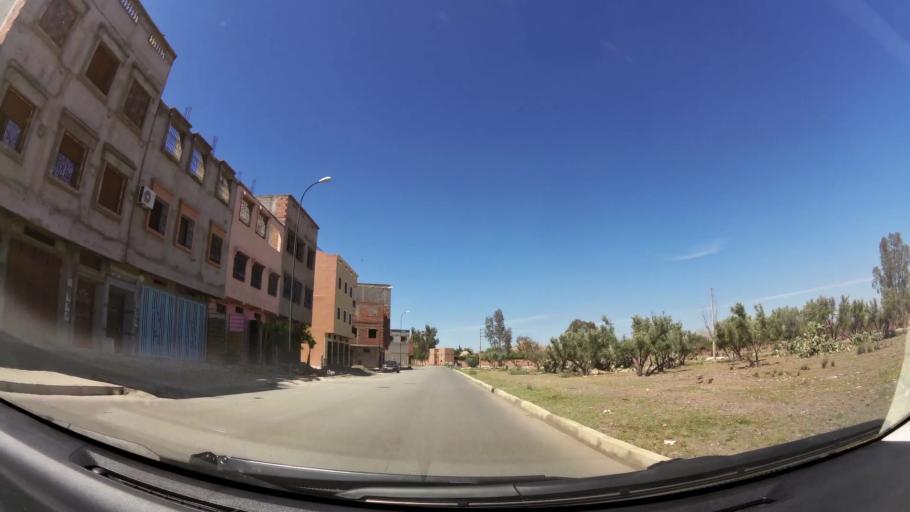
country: MA
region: Marrakech-Tensift-Al Haouz
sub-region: Marrakech
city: Marrakesh
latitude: 31.5550
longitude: -7.9786
